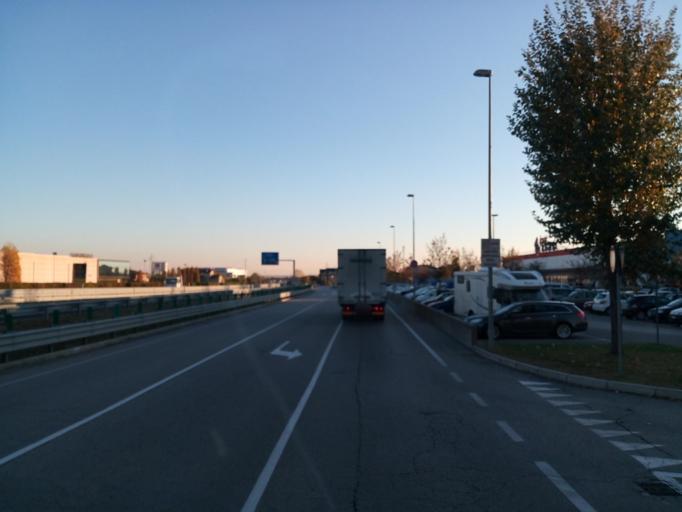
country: IT
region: Veneto
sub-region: Provincia di Vicenza
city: San Zeno-San Giuseppe
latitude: 45.7665
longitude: 11.7671
